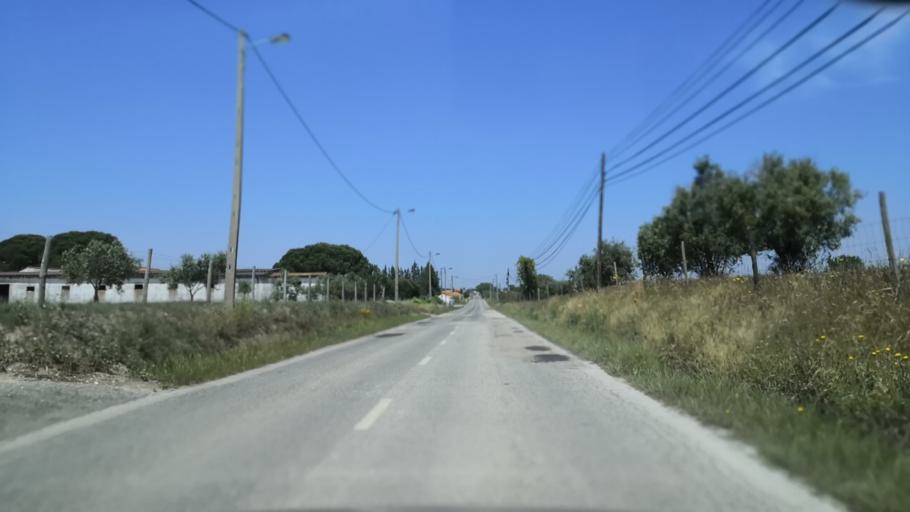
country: PT
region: Setubal
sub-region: Palmela
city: Pinhal Novo
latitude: 38.6569
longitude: -8.7408
